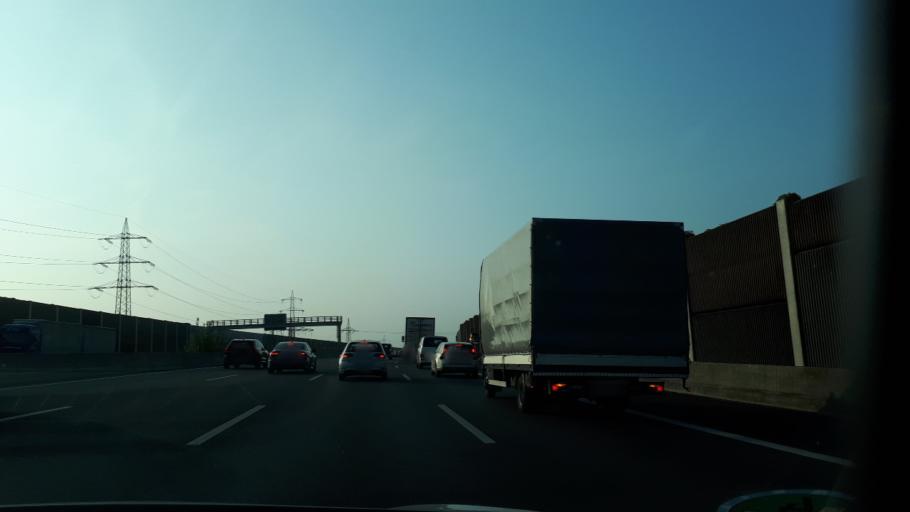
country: DE
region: North Rhine-Westphalia
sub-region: Regierungsbezirk Koln
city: Muelheim
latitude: 50.9769
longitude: 7.0255
